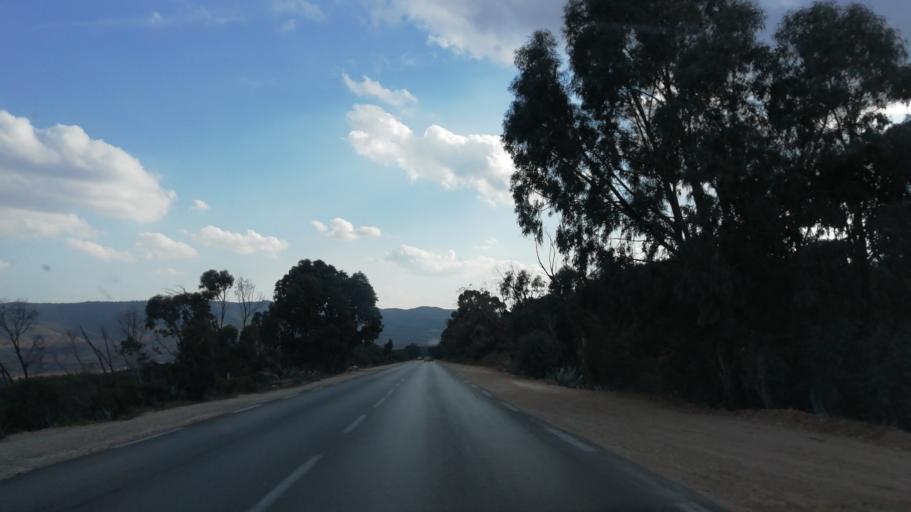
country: DZ
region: Relizane
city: Relizane
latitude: 35.9160
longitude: 0.4374
